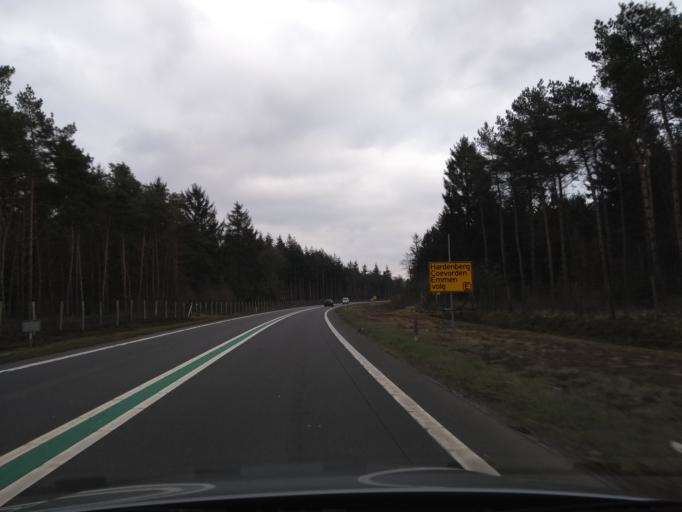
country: NL
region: Overijssel
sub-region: Gemeente Twenterand
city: Magele
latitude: 52.5604
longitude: 6.5274
